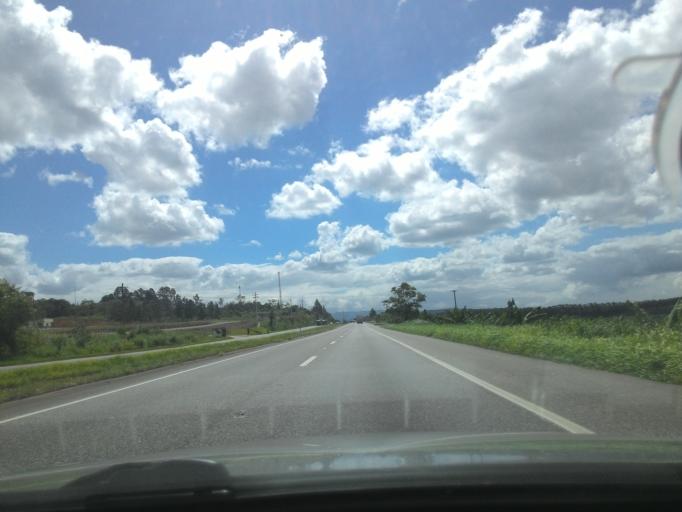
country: BR
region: Sao Paulo
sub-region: Cajati
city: Cajati
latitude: -24.7222
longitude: -48.0599
